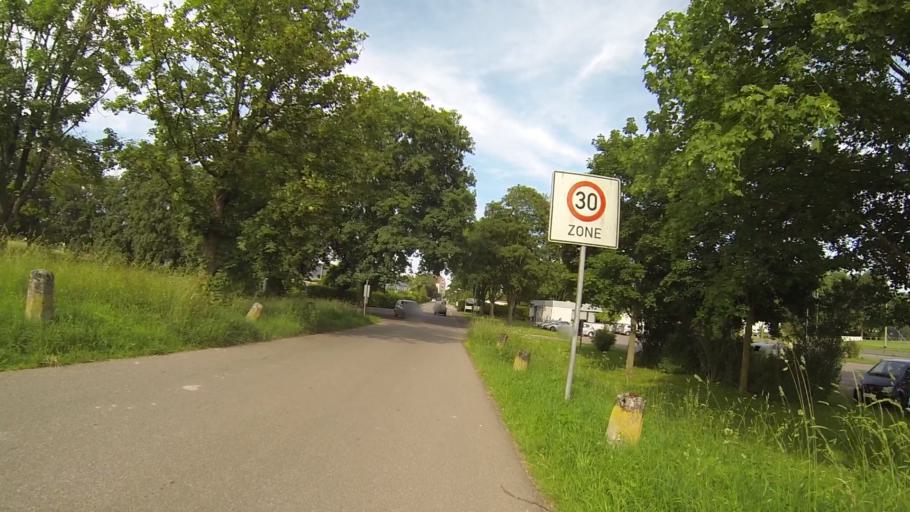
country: DE
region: Bavaria
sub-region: Swabia
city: Neu-Ulm
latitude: 48.3653
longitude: 10.0047
